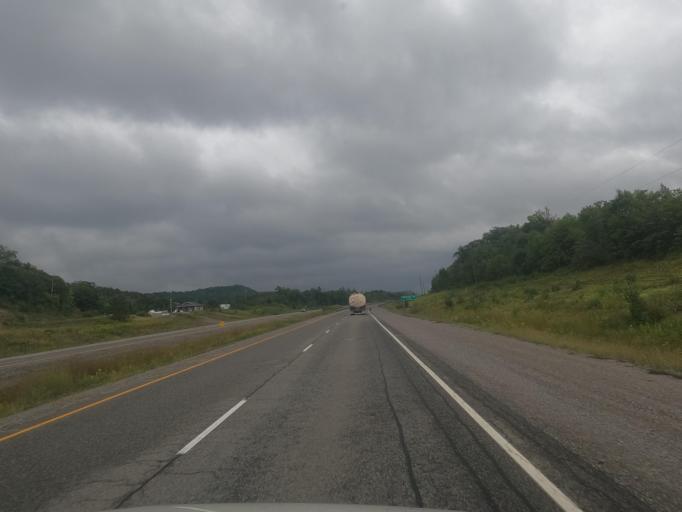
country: CA
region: Ontario
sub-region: Algoma
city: Sault Ste. Marie
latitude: 46.5488
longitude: -84.1471
